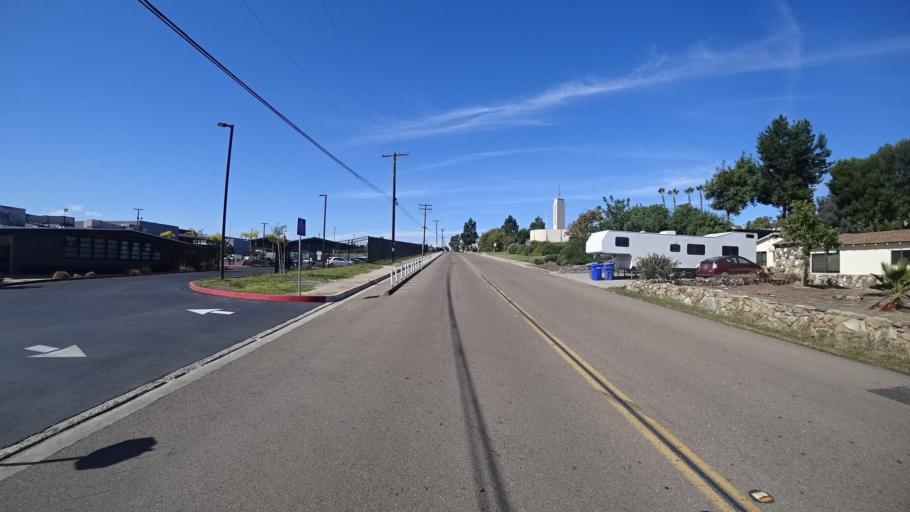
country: US
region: California
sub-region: San Diego County
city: Lemon Grove
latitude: 32.7249
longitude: -117.0162
